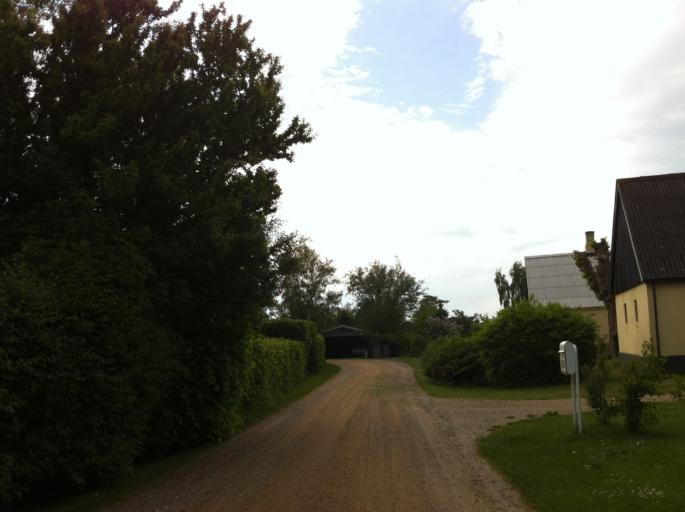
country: DK
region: Capital Region
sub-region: Gribskov Kommune
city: Gilleleje
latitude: 56.1206
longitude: 12.2611
